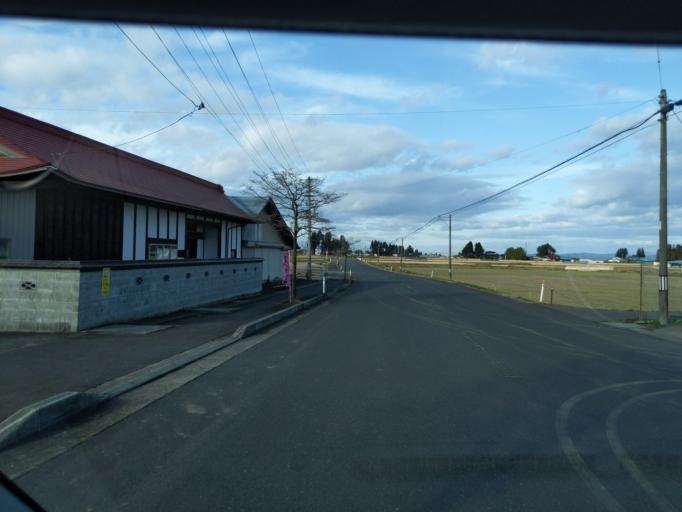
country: JP
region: Iwate
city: Mizusawa
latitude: 39.1239
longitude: 141.0922
